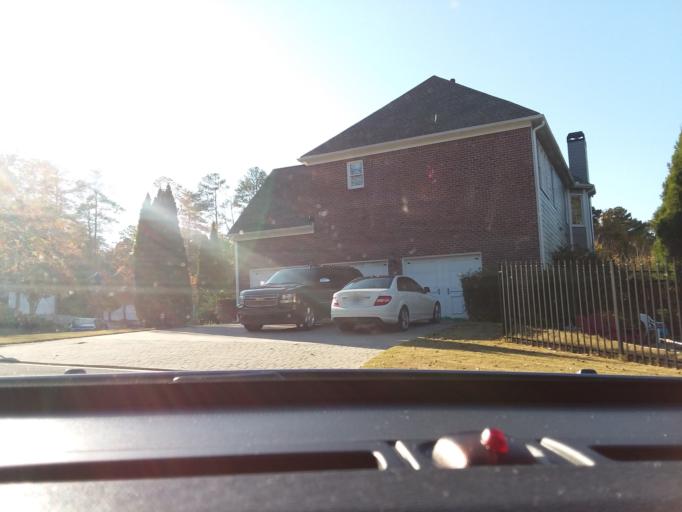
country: US
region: Georgia
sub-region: Fulton County
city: Alpharetta
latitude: 34.0324
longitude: -84.2726
